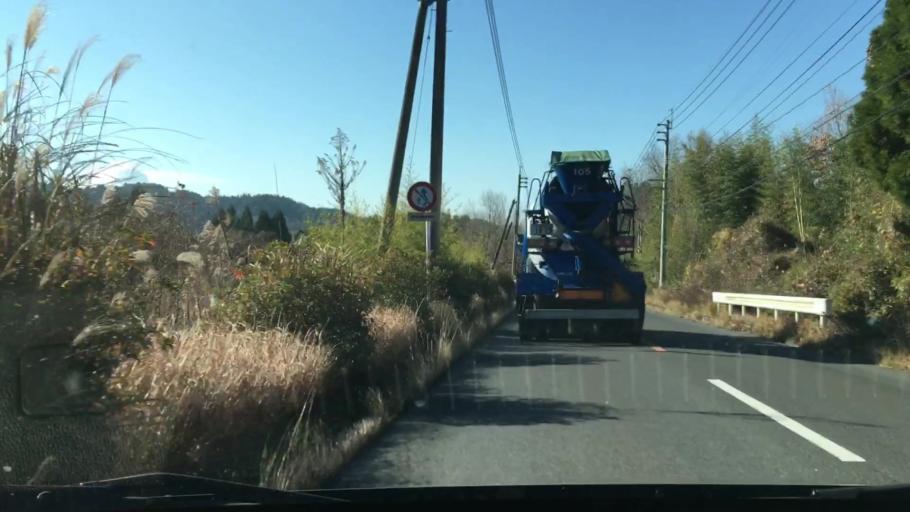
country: JP
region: Kagoshima
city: Kajiki
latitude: 31.7674
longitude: 130.6912
